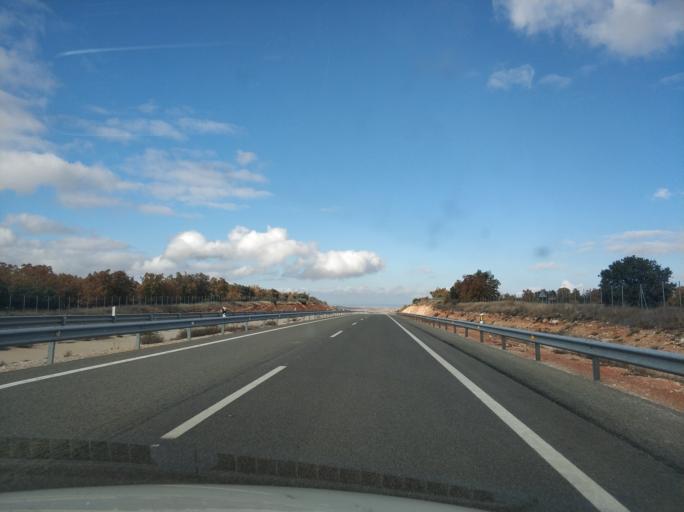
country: ES
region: Castille and Leon
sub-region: Provincia de Soria
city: Adradas
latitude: 41.3053
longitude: -2.4801
